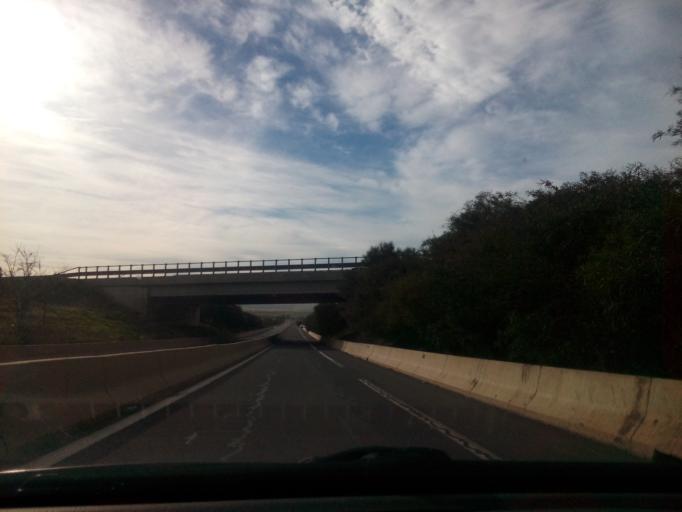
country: DZ
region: Oran
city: Sidi ech Chahmi
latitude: 35.5447
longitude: -0.3786
